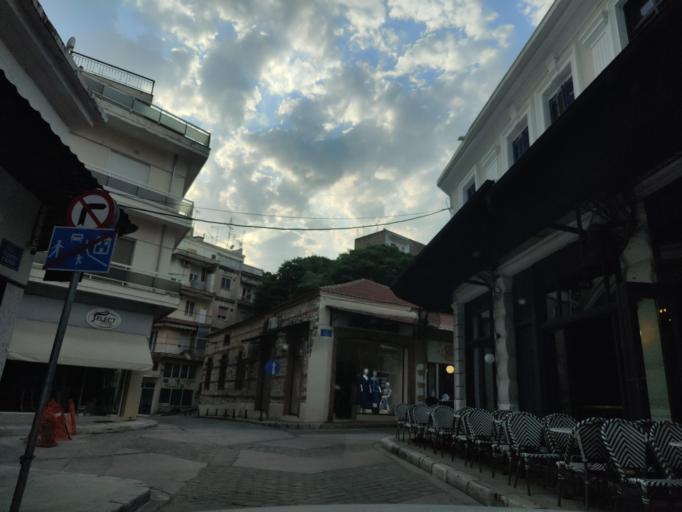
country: GR
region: East Macedonia and Thrace
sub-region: Nomos Dramas
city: Drama
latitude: 41.1499
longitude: 24.1451
